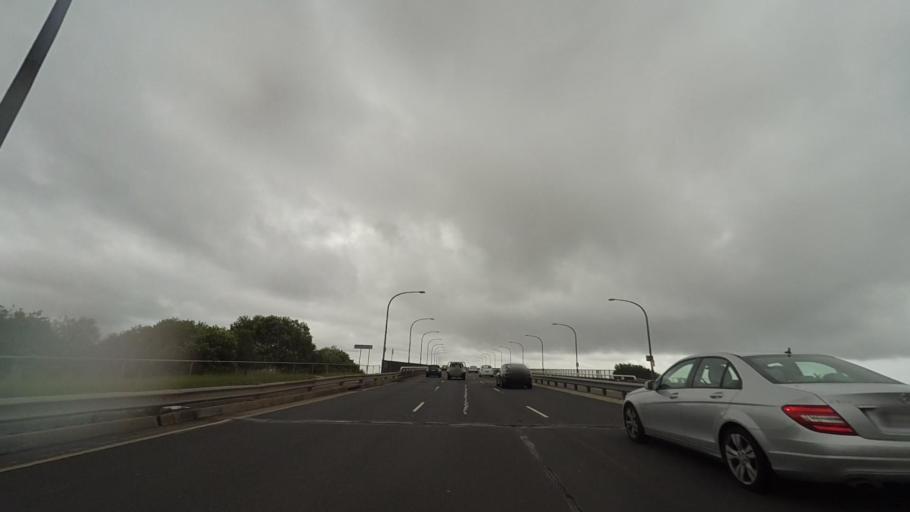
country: AU
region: New South Wales
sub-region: Rockdale
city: Dolls Point
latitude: -34.0108
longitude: 151.1264
